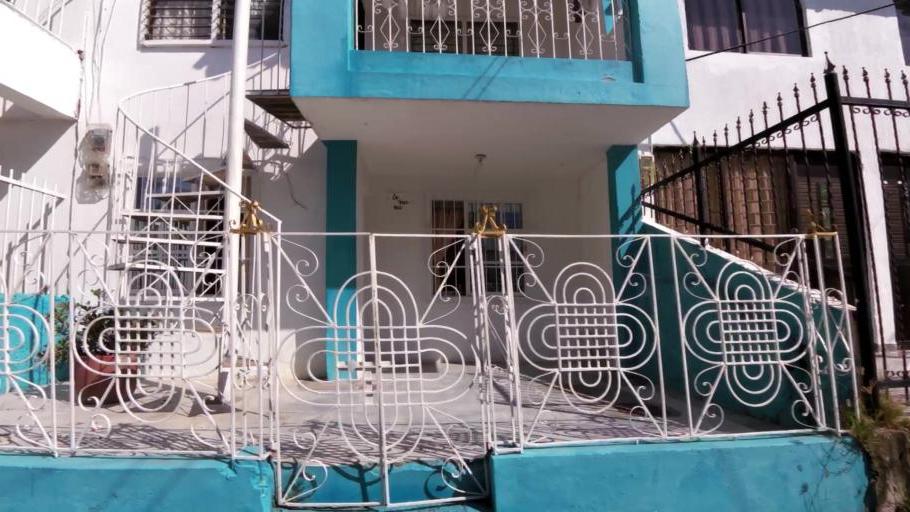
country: CO
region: Bolivar
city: Cartagena
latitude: 10.3959
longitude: -75.5164
